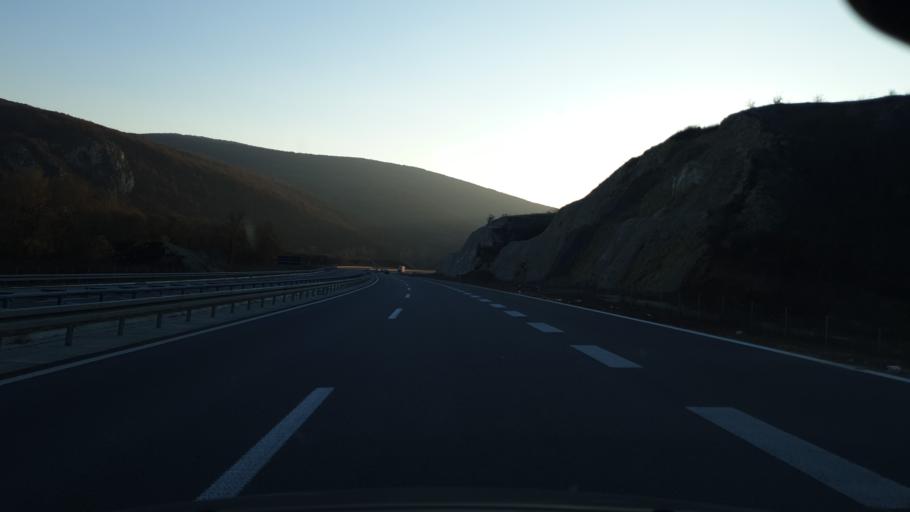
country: RS
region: Central Serbia
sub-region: Pirotski Okrug
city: Bela Palanka
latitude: 43.2279
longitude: 22.4322
